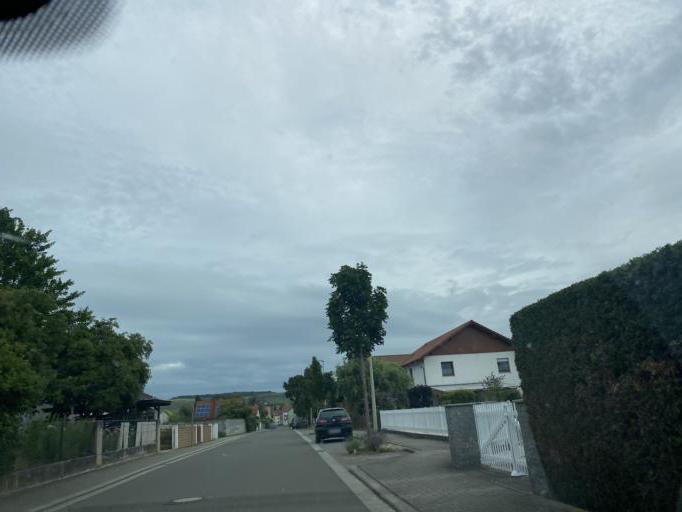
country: DE
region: Rheinland-Pfalz
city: Sprendlingen
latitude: 49.8577
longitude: 7.9904
